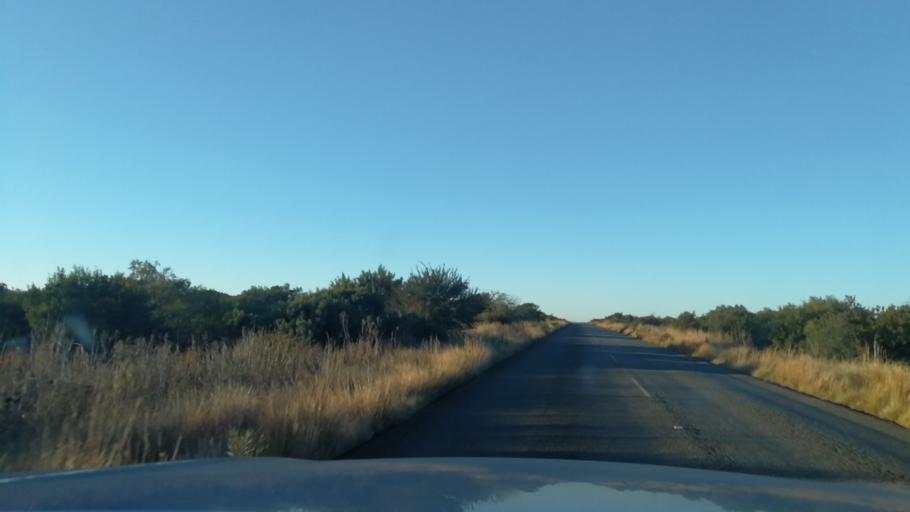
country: ZA
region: North-West
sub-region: Bojanala Platinum District Municipality
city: Koster
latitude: -25.6854
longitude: 26.7290
